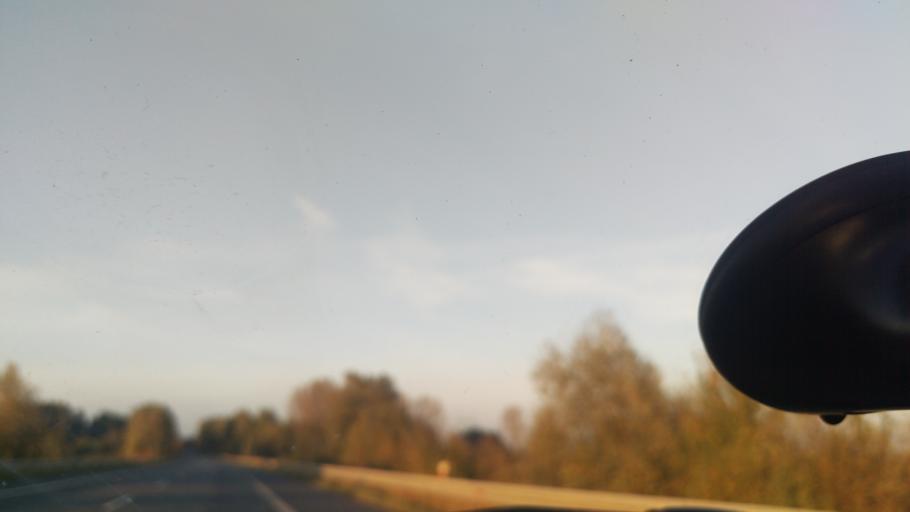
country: PL
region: West Pomeranian Voivodeship
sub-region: Powiat gryfinski
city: Stare Czarnowo
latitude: 53.2801
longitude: 14.7841
